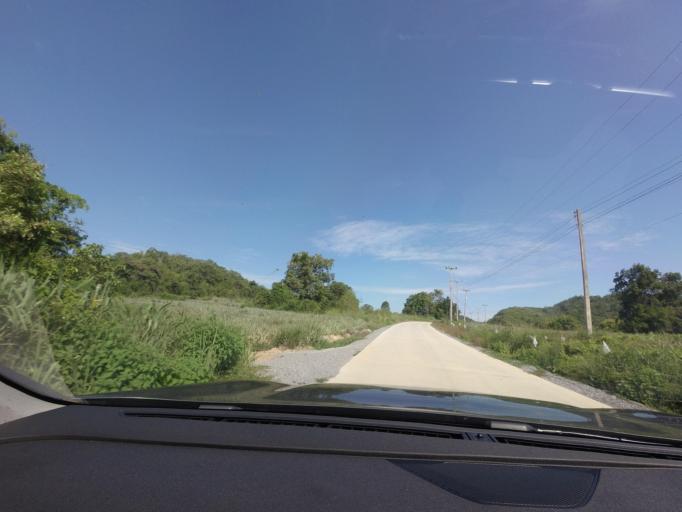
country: TH
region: Prachuap Khiri Khan
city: Pran Buri
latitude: 12.4715
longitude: 99.9411
